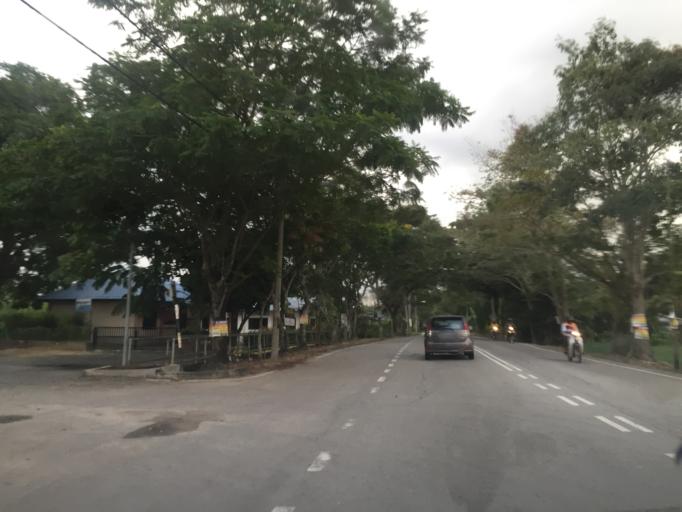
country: MY
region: Penang
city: Tasek Glugor
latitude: 5.5509
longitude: 100.5045
